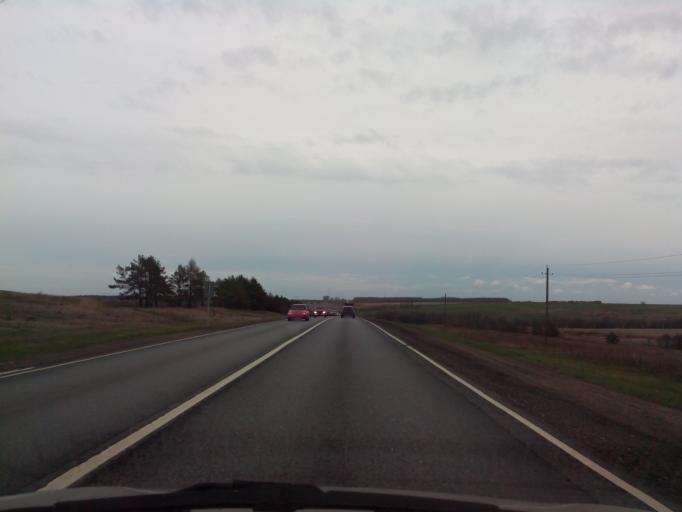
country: RU
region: Moskovskaya
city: Ozherel'ye
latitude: 54.7263
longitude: 38.2697
